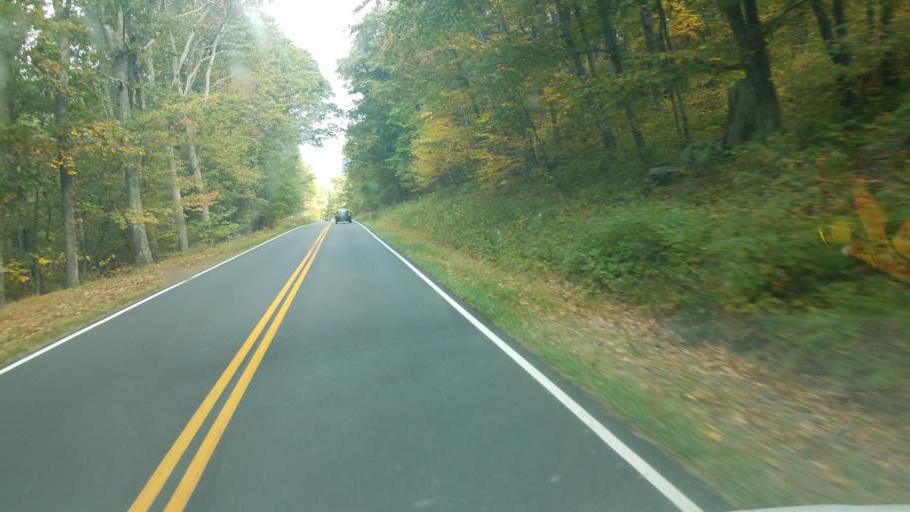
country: US
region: Virginia
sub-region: Page County
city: Luray
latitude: 38.6703
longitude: -78.3323
